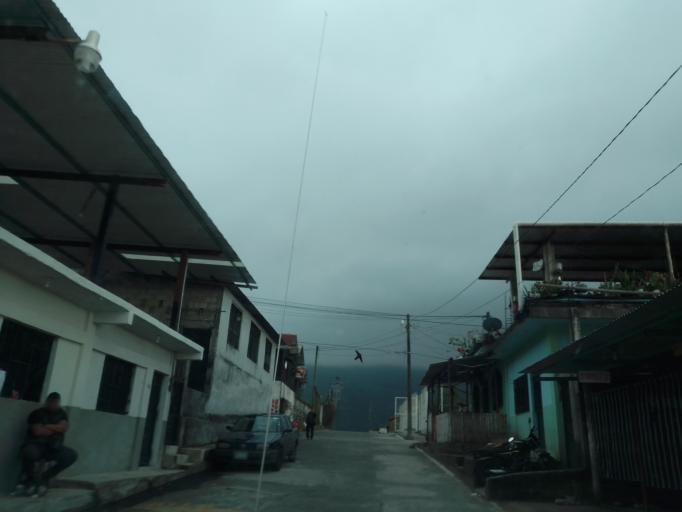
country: MX
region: Chiapas
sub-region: Union Juarez
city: Santo Domingo
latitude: 15.0599
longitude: -92.0809
